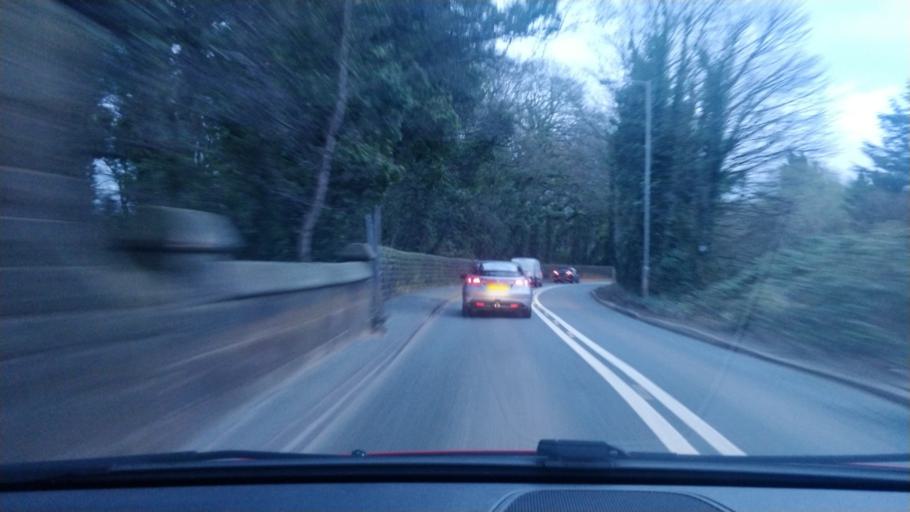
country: GB
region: England
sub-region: Knowsley
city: Knowsley
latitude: 53.4390
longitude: -2.8891
